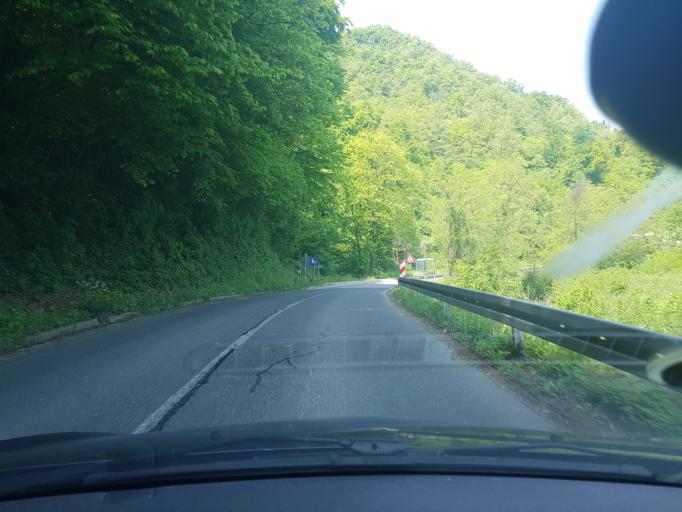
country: HR
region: Krapinsko-Zagorska
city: Pregrada
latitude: 46.1818
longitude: 15.7479
